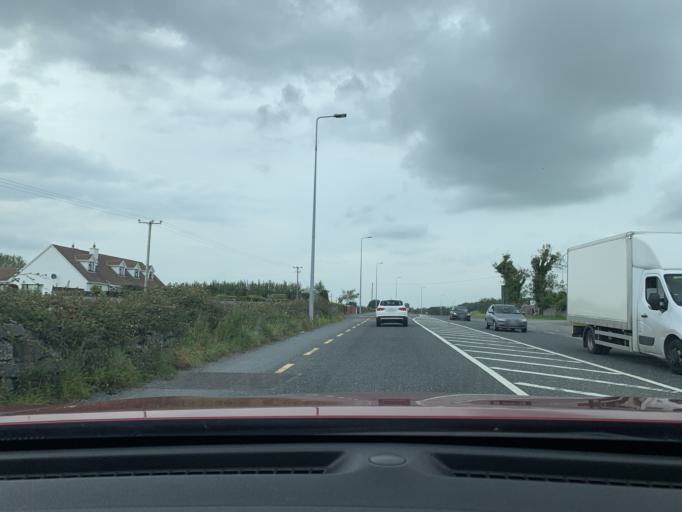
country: IE
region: Connaught
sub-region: County Galway
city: Gaillimh
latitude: 53.2971
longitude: -9.0130
